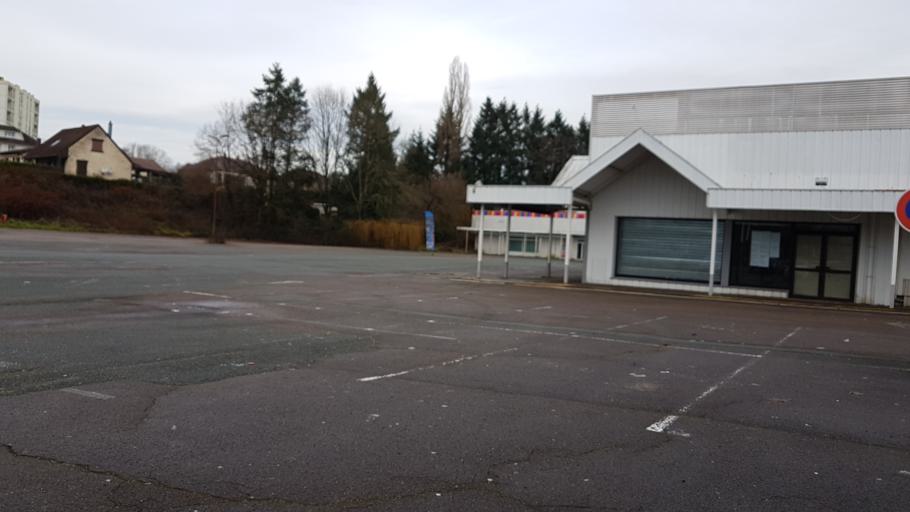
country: FR
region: Franche-Comte
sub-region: Departement de la Haute-Saone
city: Luxeuil-les-Bains
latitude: 47.8116
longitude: 6.3733
